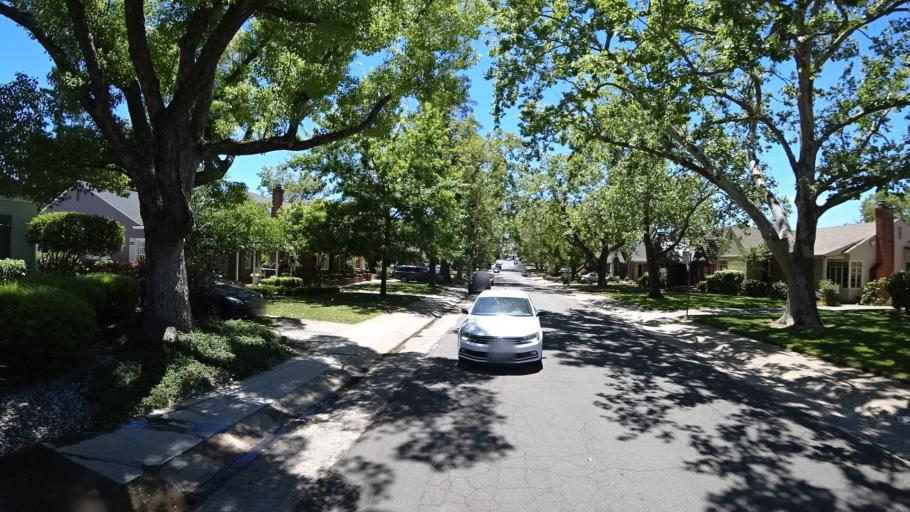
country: US
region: California
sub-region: Sacramento County
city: Sacramento
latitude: 38.5709
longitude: -121.4423
